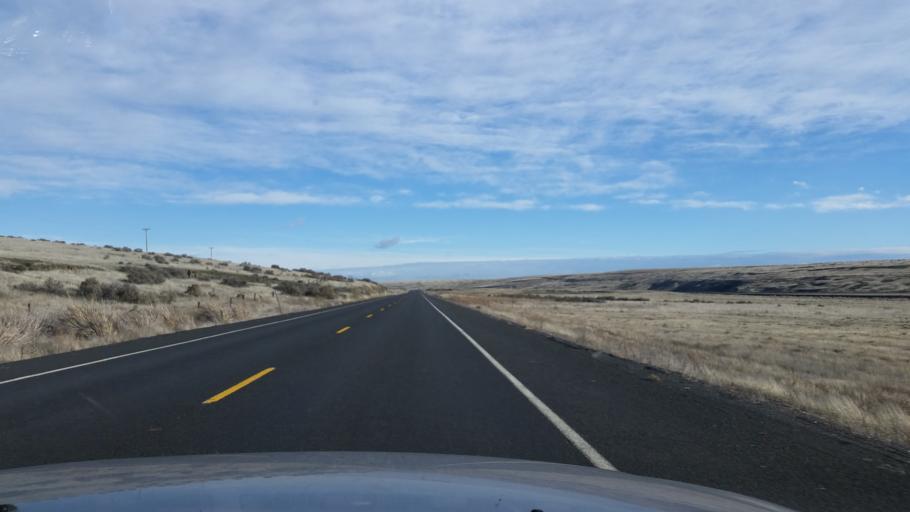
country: US
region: Washington
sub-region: Adams County
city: Ritzville
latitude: 47.3477
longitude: -118.5739
